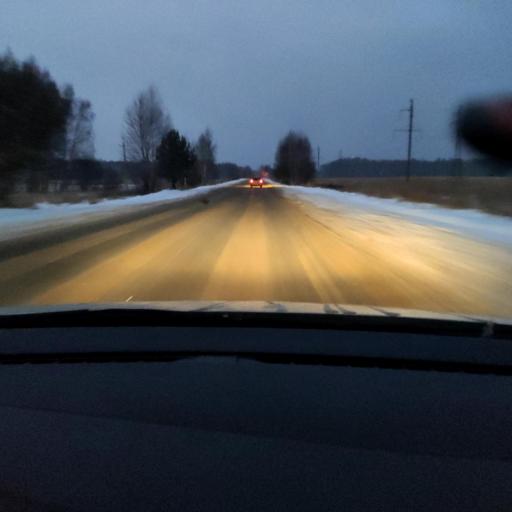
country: RU
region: Tatarstan
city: Aysha
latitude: 55.8642
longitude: 48.5835
